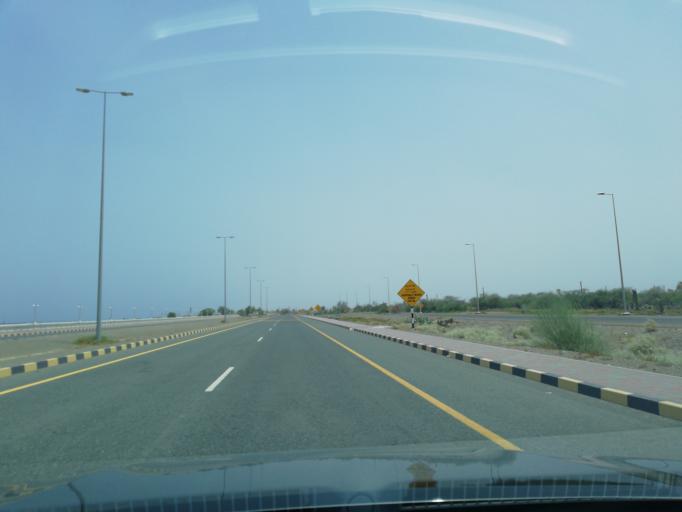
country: OM
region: Al Batinah
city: Al Liwa'
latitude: 24.6240
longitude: 56.5315
